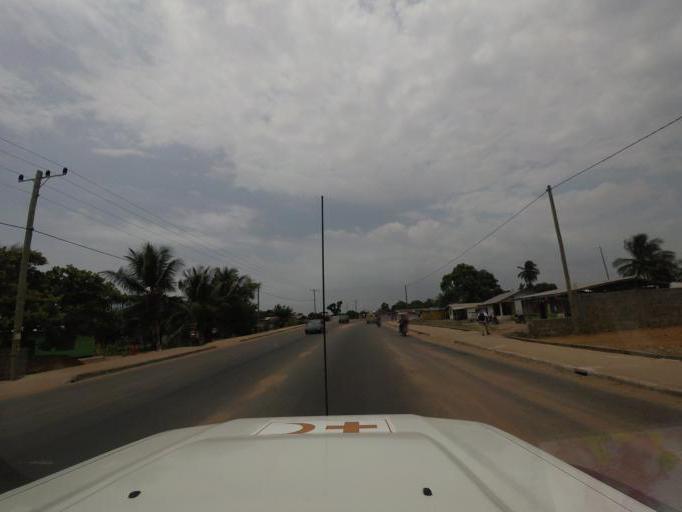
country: LR
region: Montserrado
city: Monrovia
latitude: 6.2900
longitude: -10.7171
